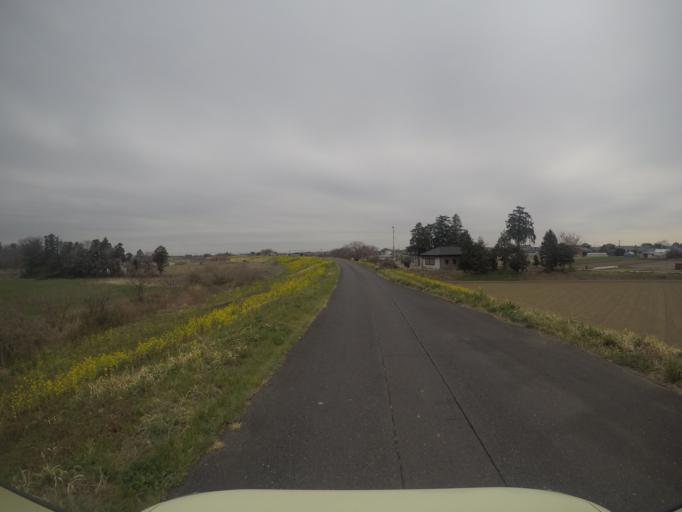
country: JP
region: Ibaraki
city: Ishige
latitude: 36.0918
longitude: 139.9975
